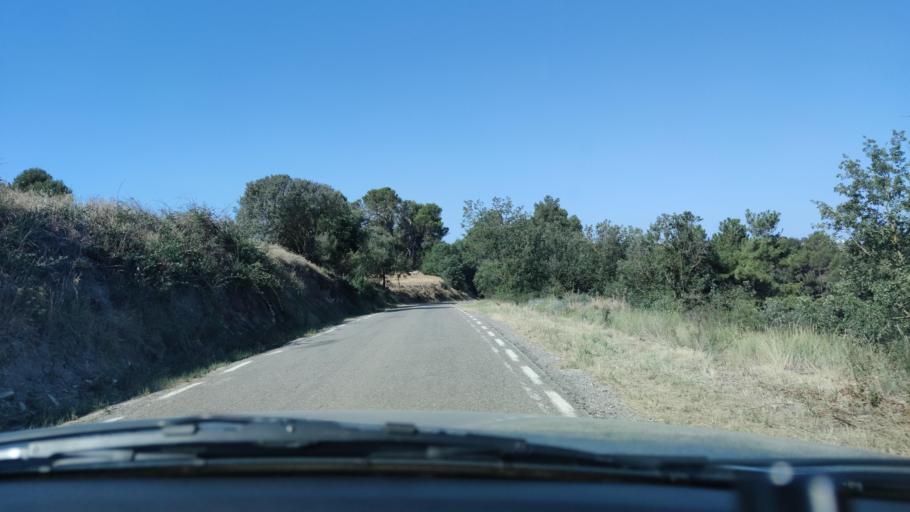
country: ES
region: Catalonia
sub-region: Provincia de Barcelona
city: Pujalt
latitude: 41.6953
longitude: 1.3786
